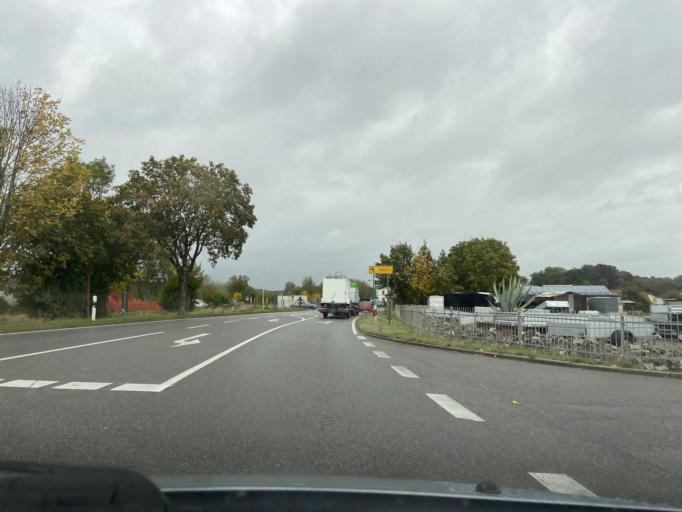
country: DE
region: Baden-Wuerttemberg
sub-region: Tuebingen Region
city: Krauchenwies
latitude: 48.0174
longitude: 9.2359
